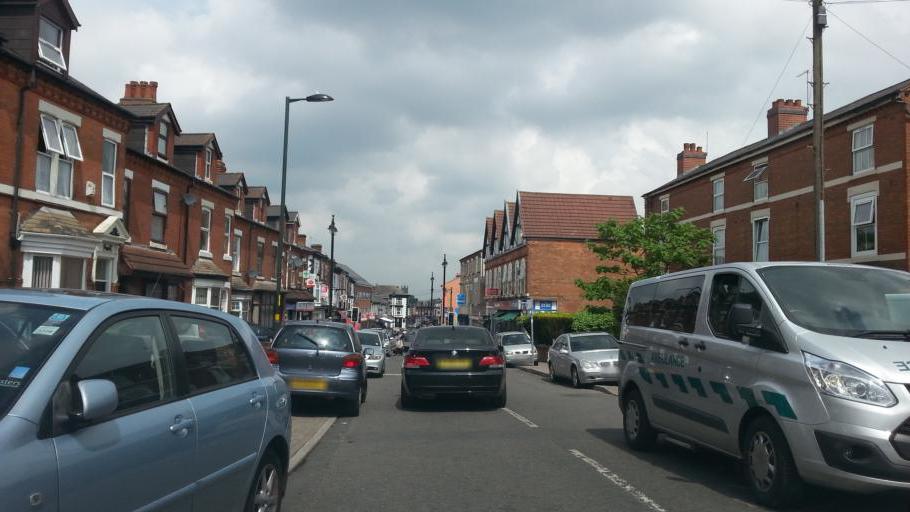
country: GB
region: England
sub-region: City and Borough of Birmingham
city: Birmingham
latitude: 52.4513
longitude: -1.8792
